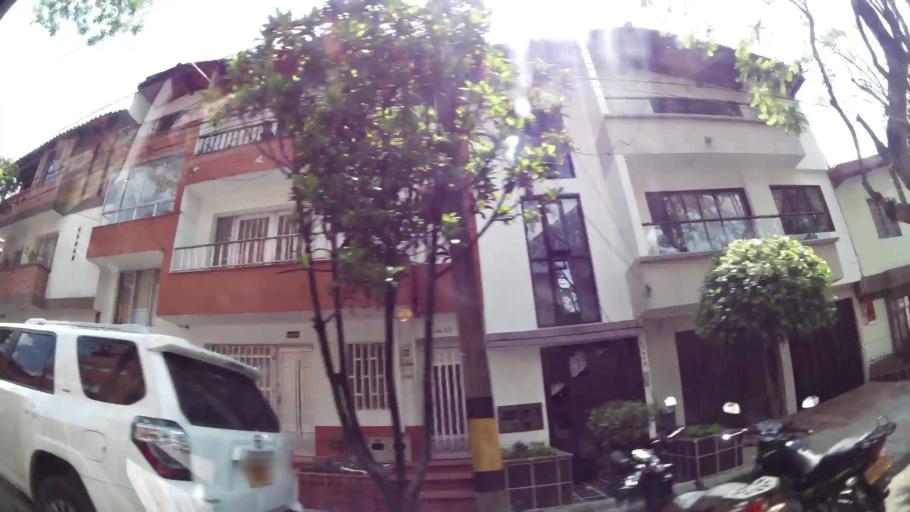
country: CO
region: Antioquia
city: Envigado
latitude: 6.1730
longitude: -75.5884
